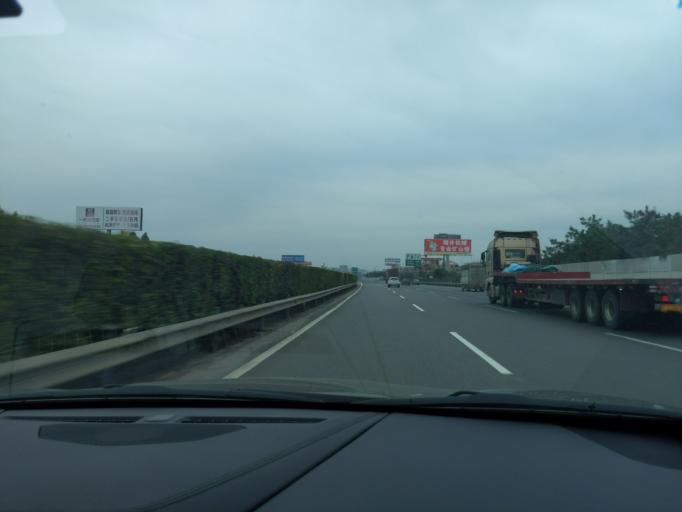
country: CN
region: Fujian
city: Anhai
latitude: 24.7352
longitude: 118.4211
